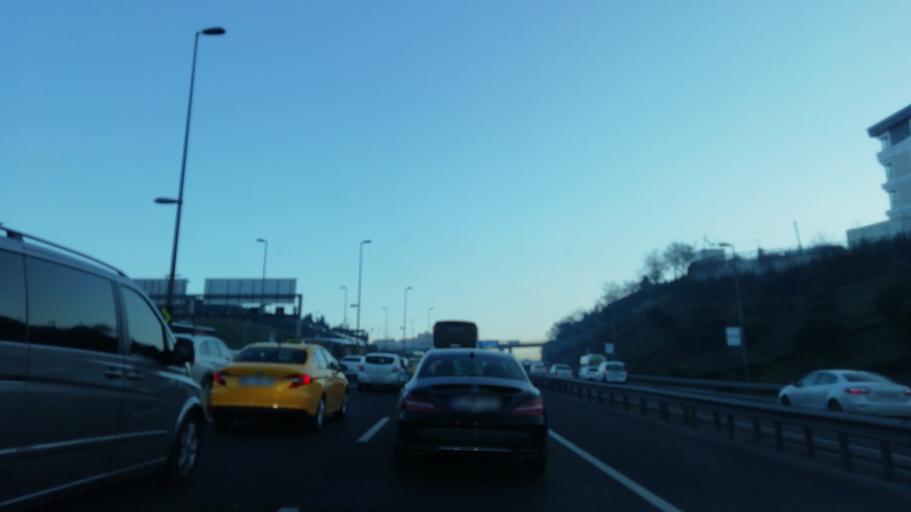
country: TR
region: Istanbul
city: Istanbul
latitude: 41.0506
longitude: 28.9490
